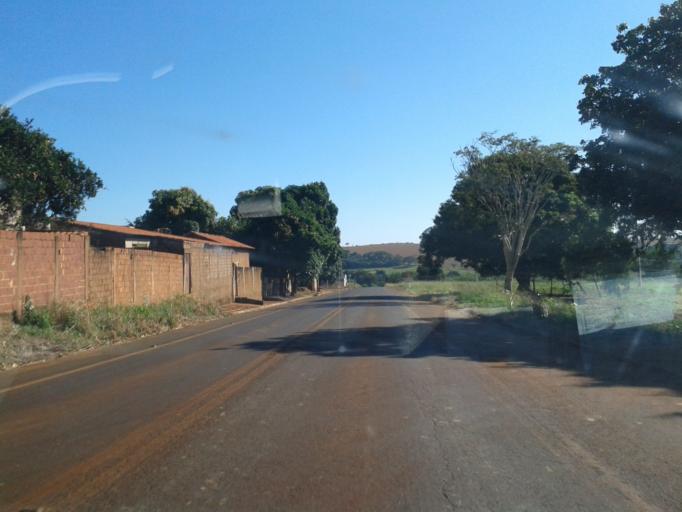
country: BR
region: Minas Gerais
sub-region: Capinopolis
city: Capinopolis
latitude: -18.6848
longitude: -49.5636
